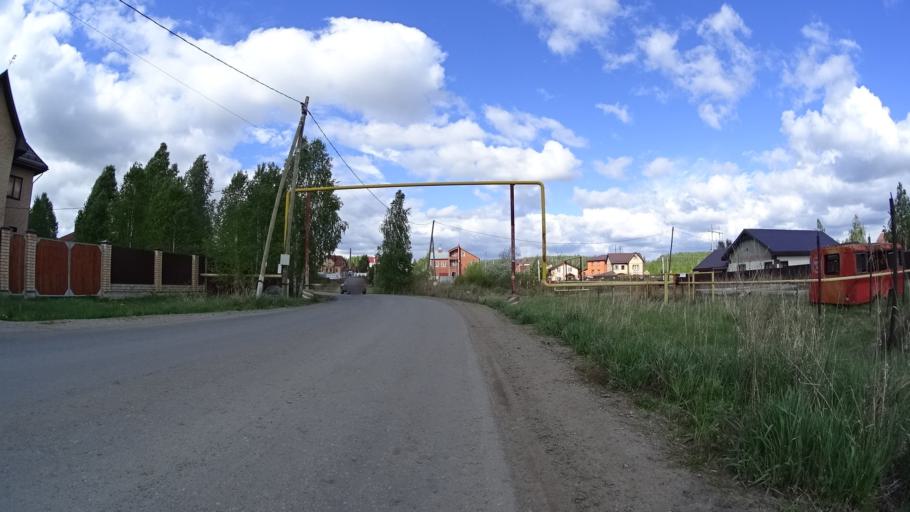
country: RU
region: Chelyabinsk
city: Sargazy
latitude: 55.1547
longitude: 61.2410
